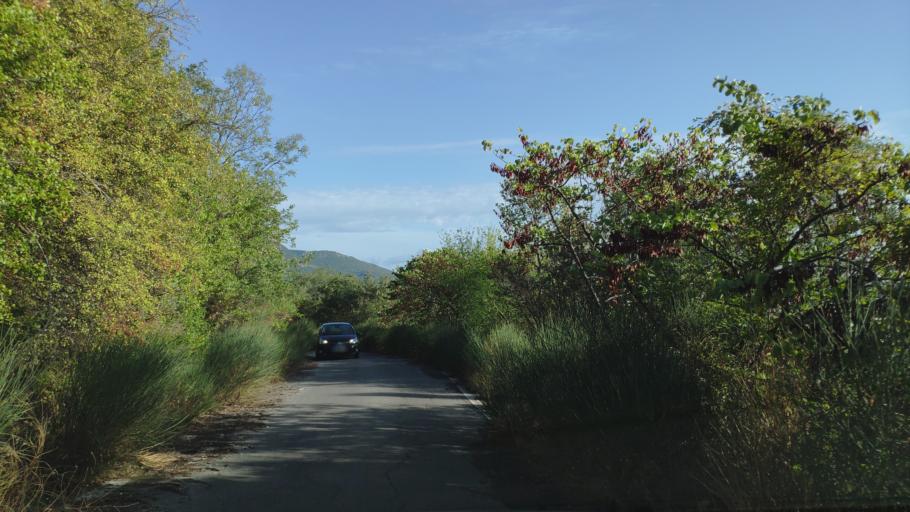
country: GR
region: Peloponnese
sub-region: Nomos Arkadias
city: Dimitsana
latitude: 37.5506
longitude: 22.0430
